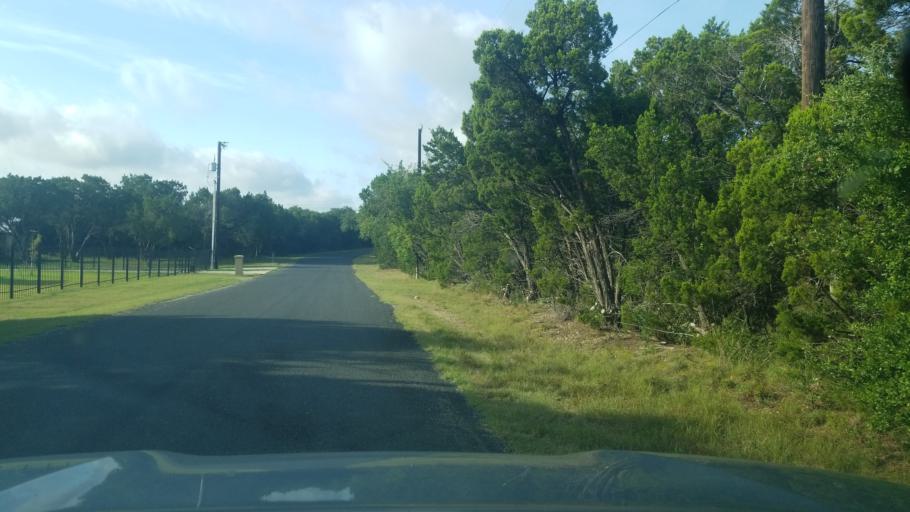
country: US
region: Texas
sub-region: Bexar County
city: Timberwood Park
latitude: 29.6989
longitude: -98.5181
